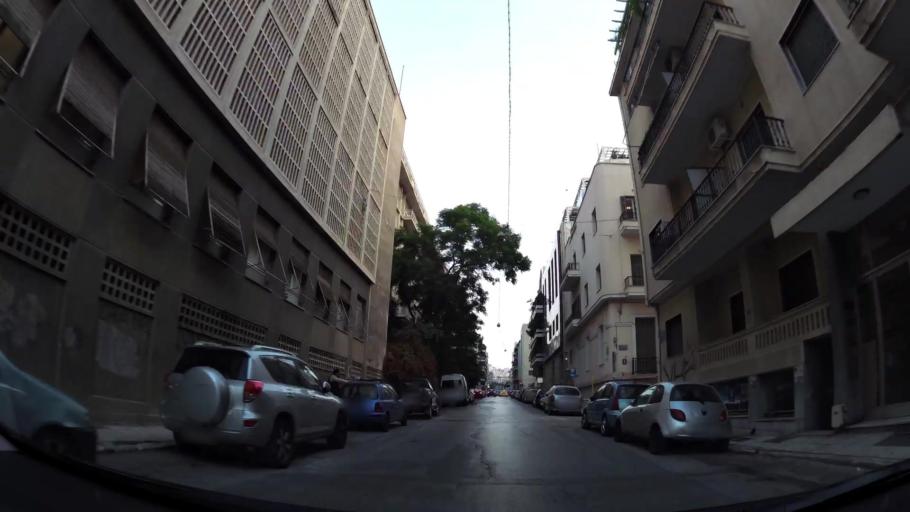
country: GR
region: Attica
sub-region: Nomarchia Athinas
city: Kaisariani
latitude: 37.9843
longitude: 23.7568
